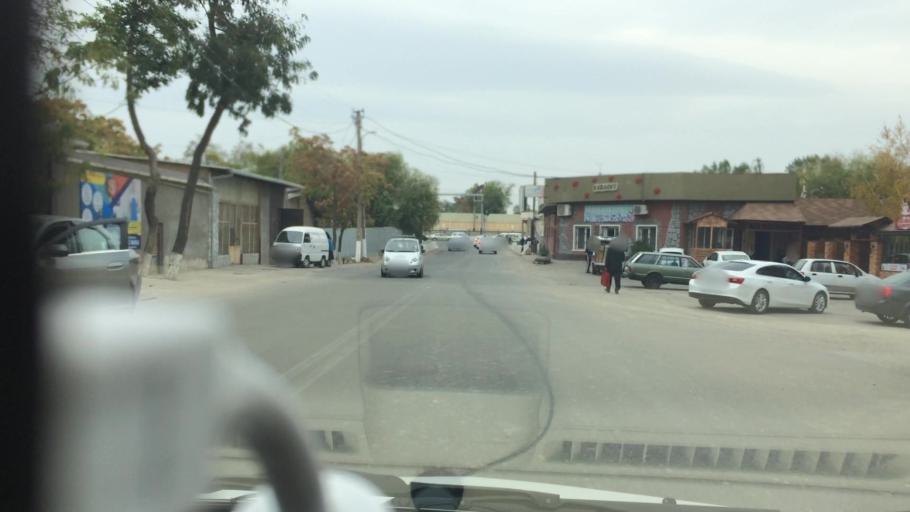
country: UZ
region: Toshkent Shahri
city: Tashkent
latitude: 41.2789
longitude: 69.2711
